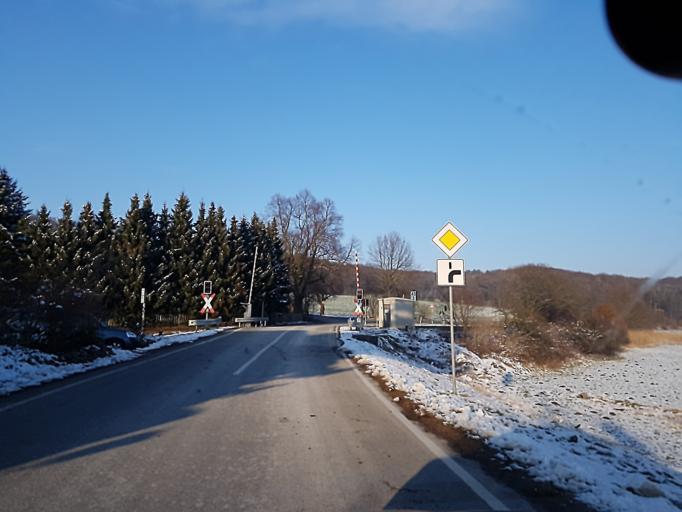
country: DE
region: Saxony
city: Bockelwitz
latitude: 51.1562
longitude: 12.9889
